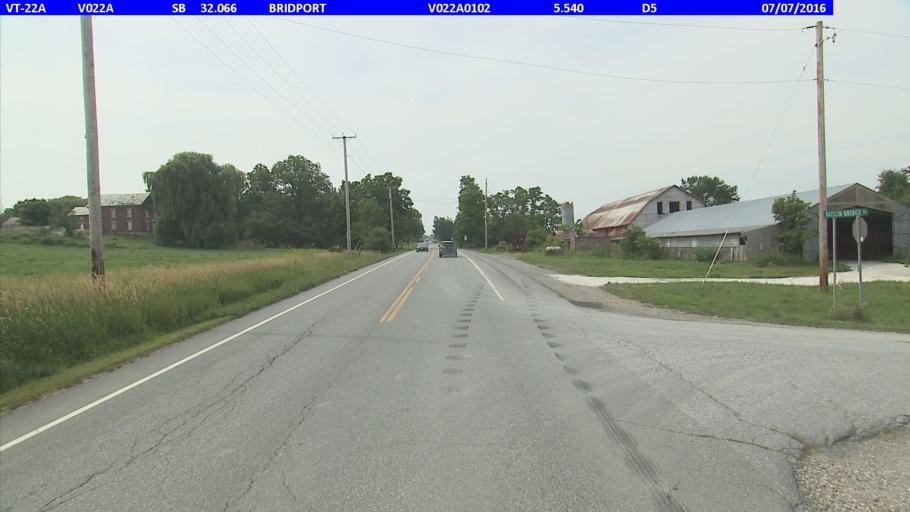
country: US
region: Vermont
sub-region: Addison County
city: Middlebury (village)
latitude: 44.0195
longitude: -73.3109
